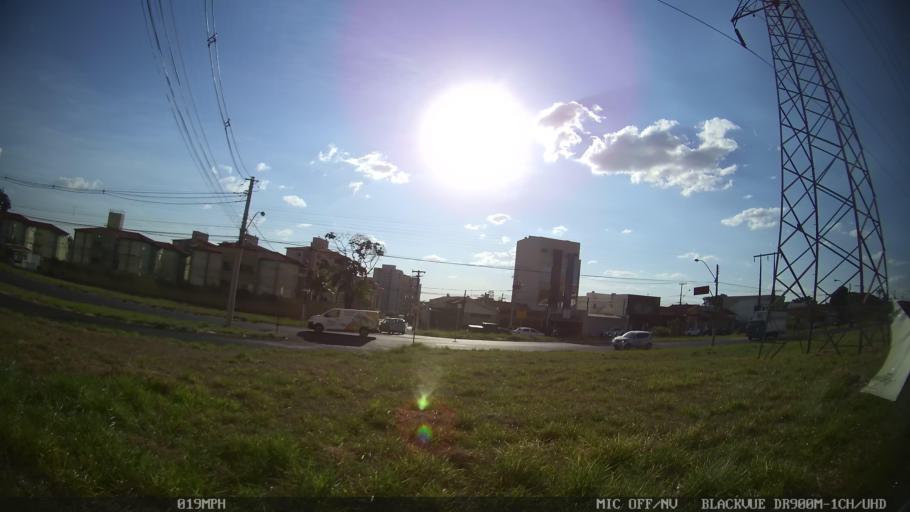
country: BR
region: Sao Paulo
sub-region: Ribeirao Preto
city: Ribeirao Preto
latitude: -21.1970
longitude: -47.7785
